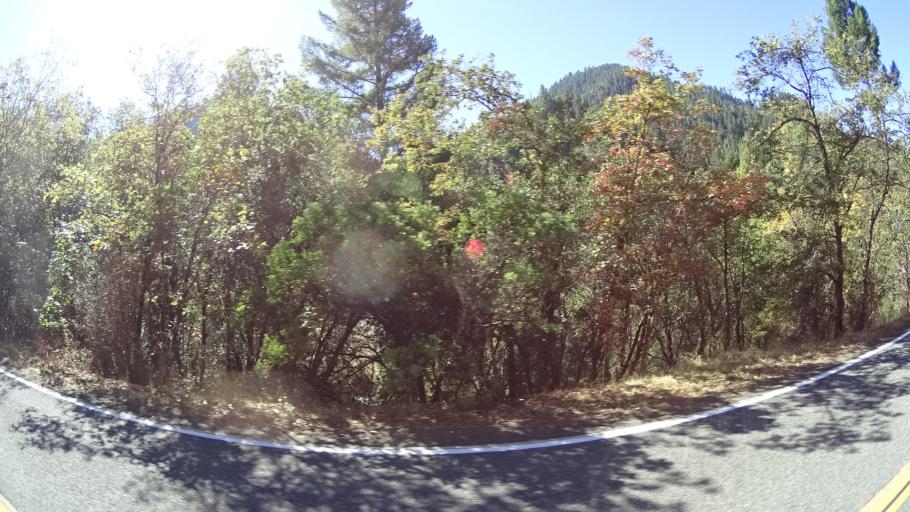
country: US
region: California
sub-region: Siskiyou County
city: Happy Camp
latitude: 41.3766
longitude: -123.4544
